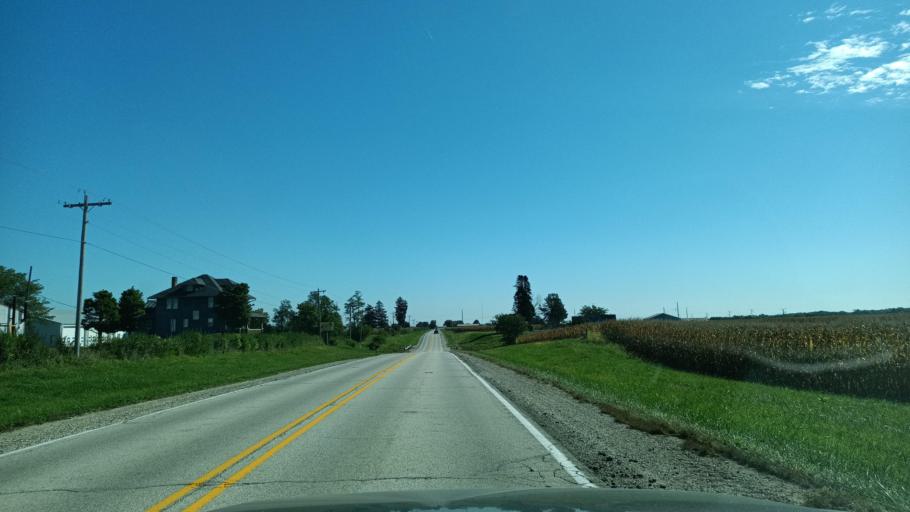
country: US
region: Illinois
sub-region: Knox County
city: Knoxville
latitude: 40.9089
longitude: -90.2259
